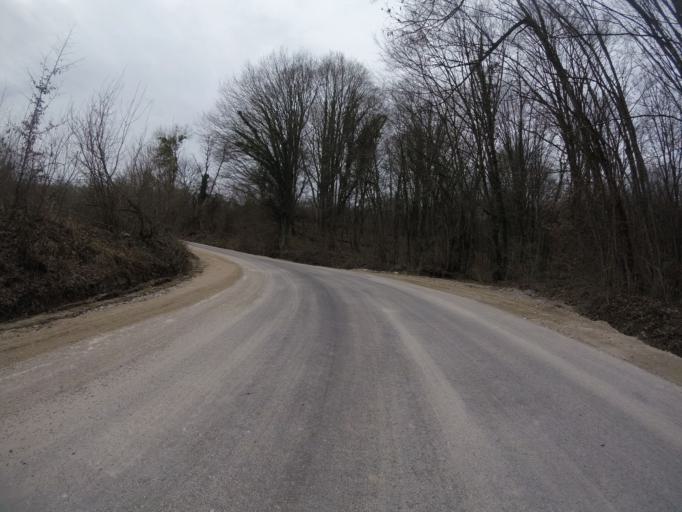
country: HR
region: Grad Zagreb
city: Strmec
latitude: 45.6031
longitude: 15.9072
